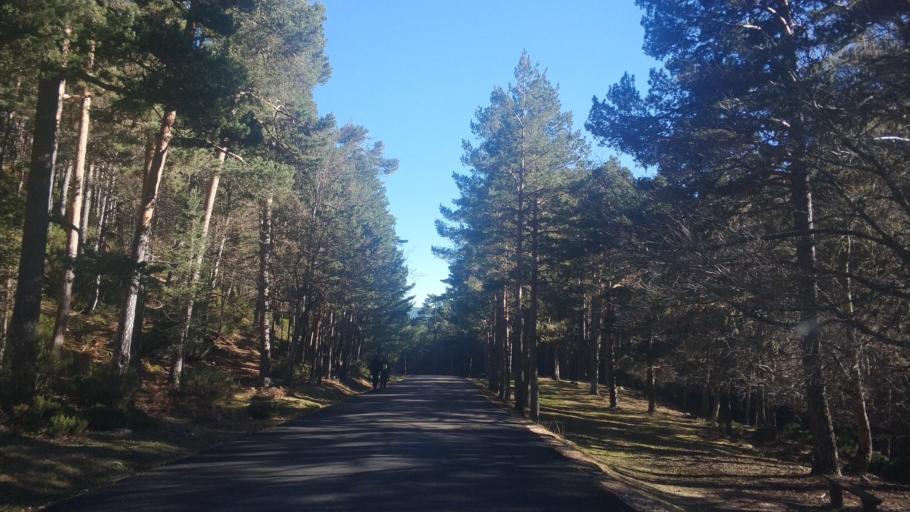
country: ES
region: Castille and Leon
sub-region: Provincia de Soria
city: Covaleda
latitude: 41.9975
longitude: -2.8357
